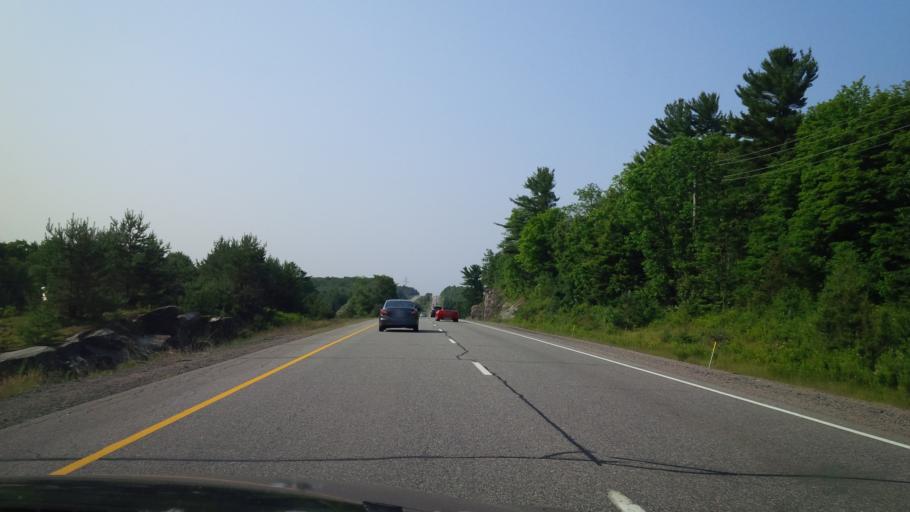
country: CA
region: Ontario
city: Bracebridge
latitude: 45.1732
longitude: -79.3121
